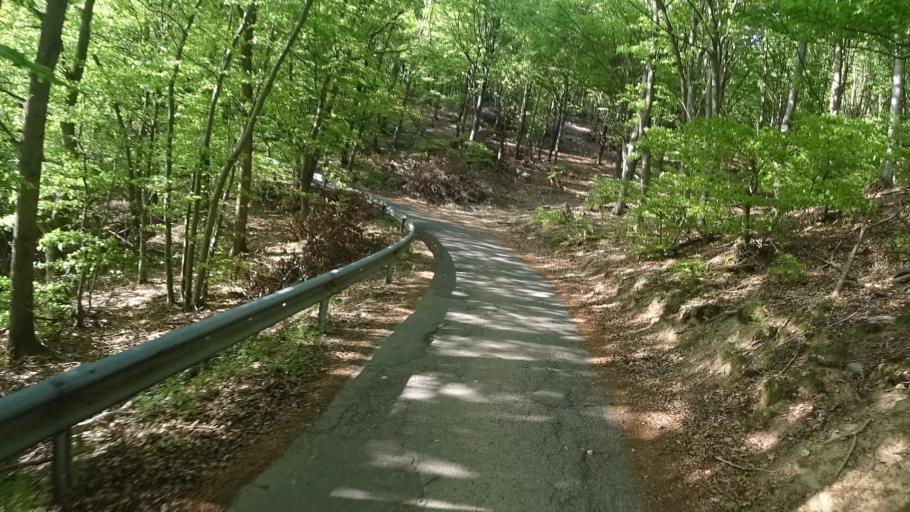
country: DE
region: Rheinland-Pfalz
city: Kirchsahr
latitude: 50.5082
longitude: 6.8713
